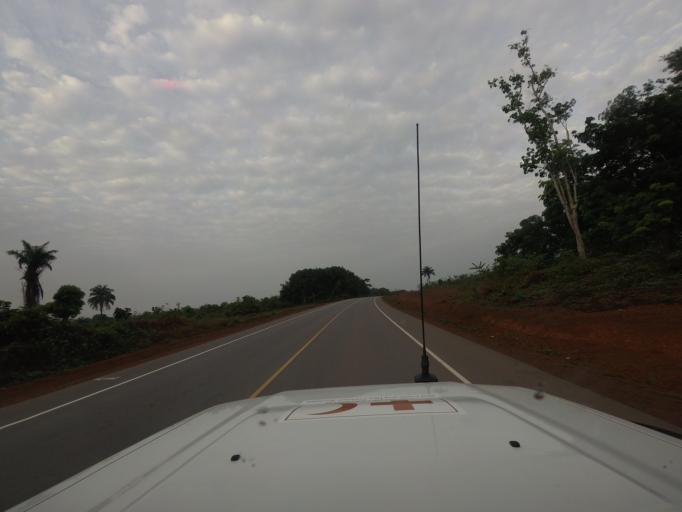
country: LR
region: Nimba
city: Sanniquellie
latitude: 7.1831
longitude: -9.0263
